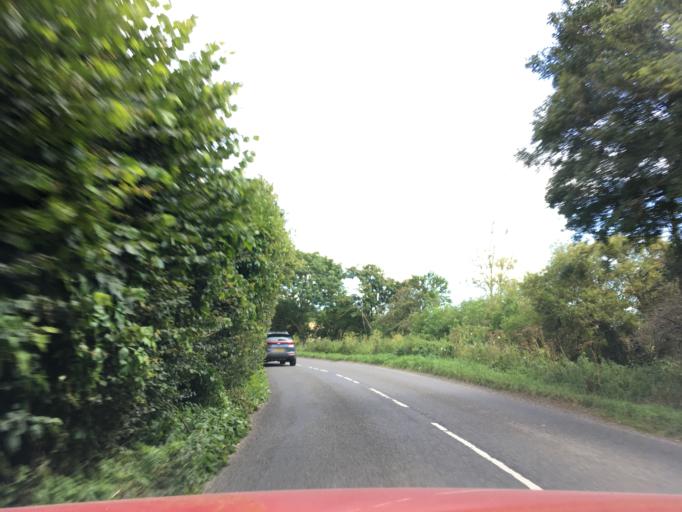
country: GB
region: England
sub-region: Somerset
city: Ilchester
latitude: 51.0507
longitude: -2.6692
